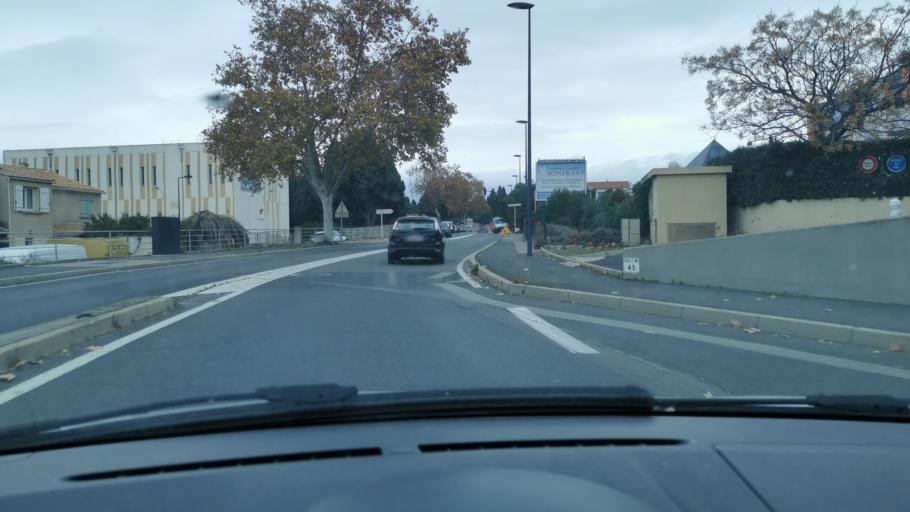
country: FR
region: Languedoc-Roussillon
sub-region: Departement de l'Herault
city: Sete
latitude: 43.4025
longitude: 3.6620
